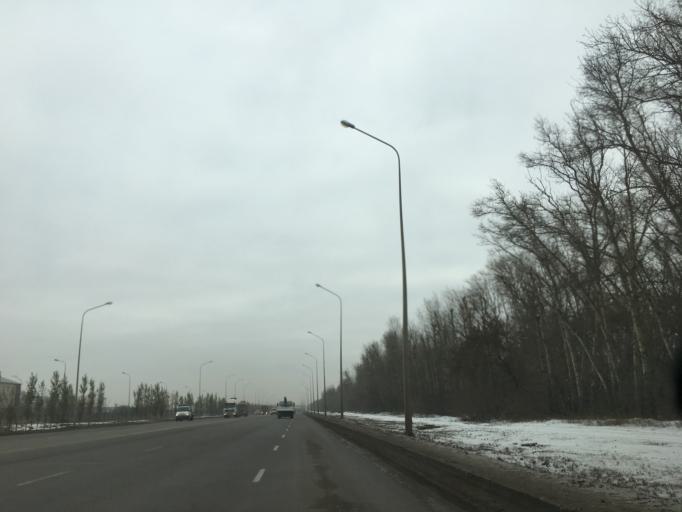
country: KZ
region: Astana Qalasy
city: Astana
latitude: 51.1670
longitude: 71.5011
